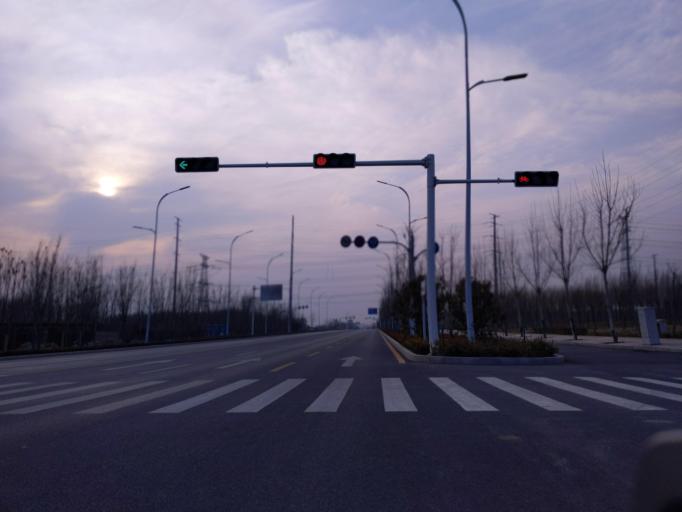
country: CN
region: Henan Sheng
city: Puyang
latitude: 35.8187
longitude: 115.0006
